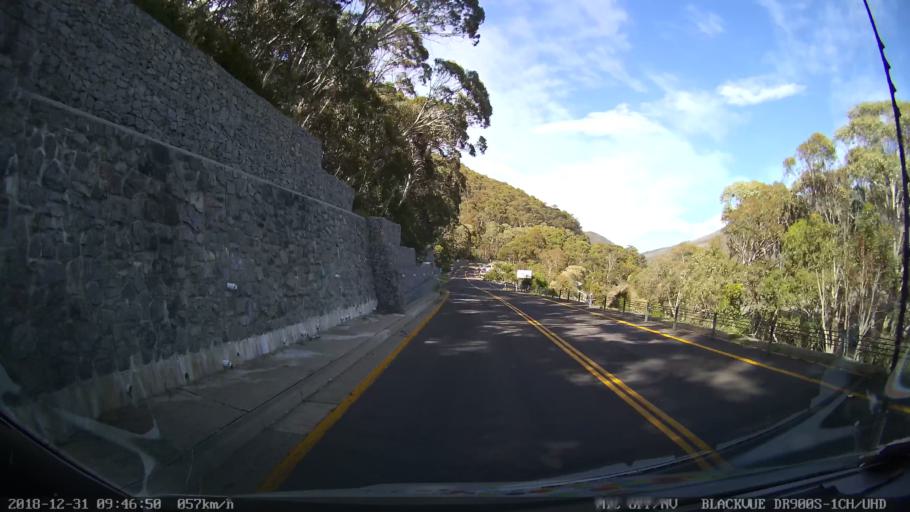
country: AU
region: New South Wales
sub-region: Snowy River
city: Jindabyne
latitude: -36.5058
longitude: 148.3064
